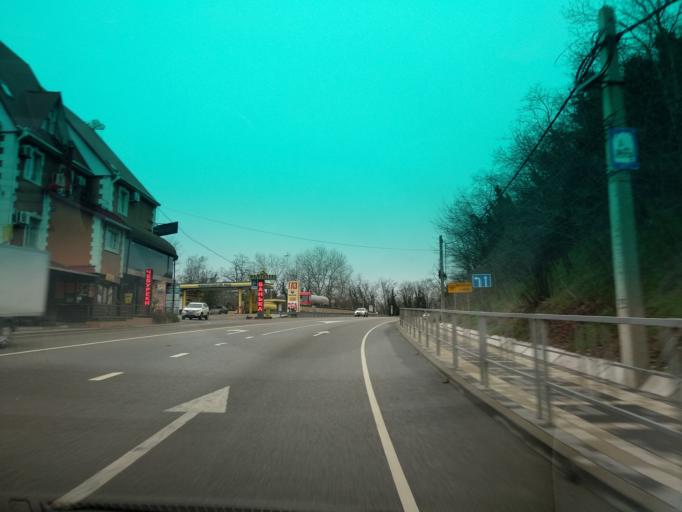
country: RU
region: Krasnodarskiy
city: Tuapse
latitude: 44.1057
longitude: 39.0752
